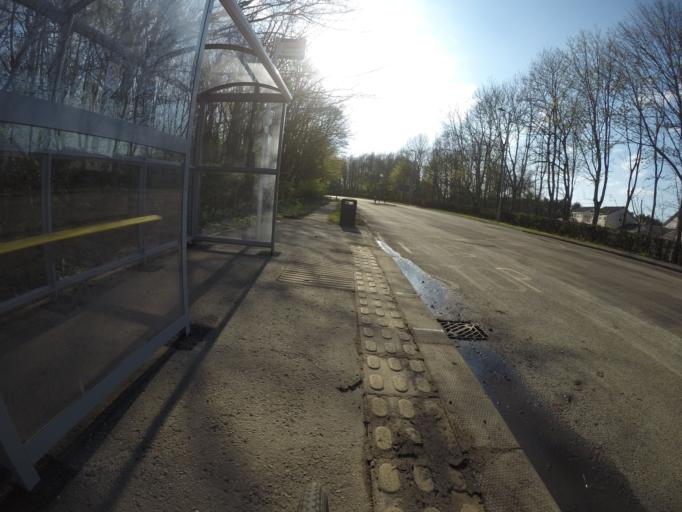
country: GB
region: Scotland
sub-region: North Ayrshire
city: Kilwinning
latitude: 55.6500
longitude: -4.7245
